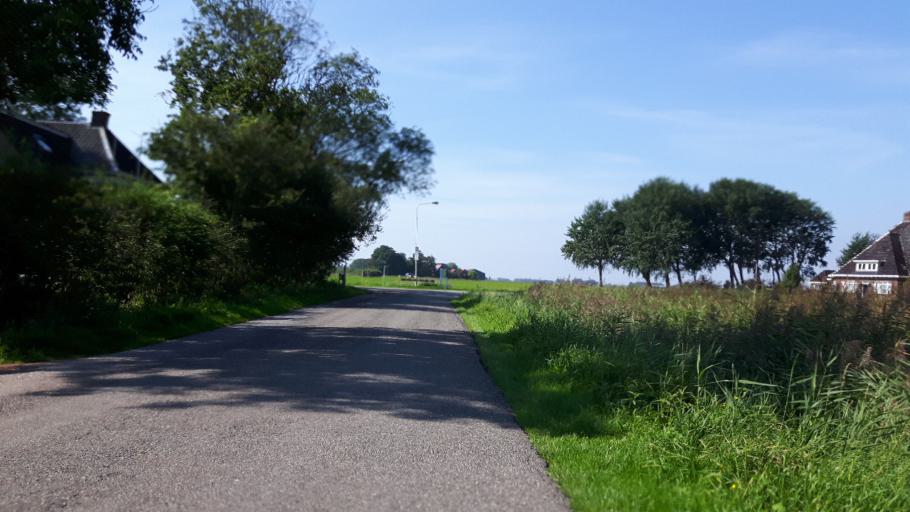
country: NL
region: Friesland
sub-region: Gemeente Ferwerderadiel
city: Ferwert
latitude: 53.3512
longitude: 5.8528
